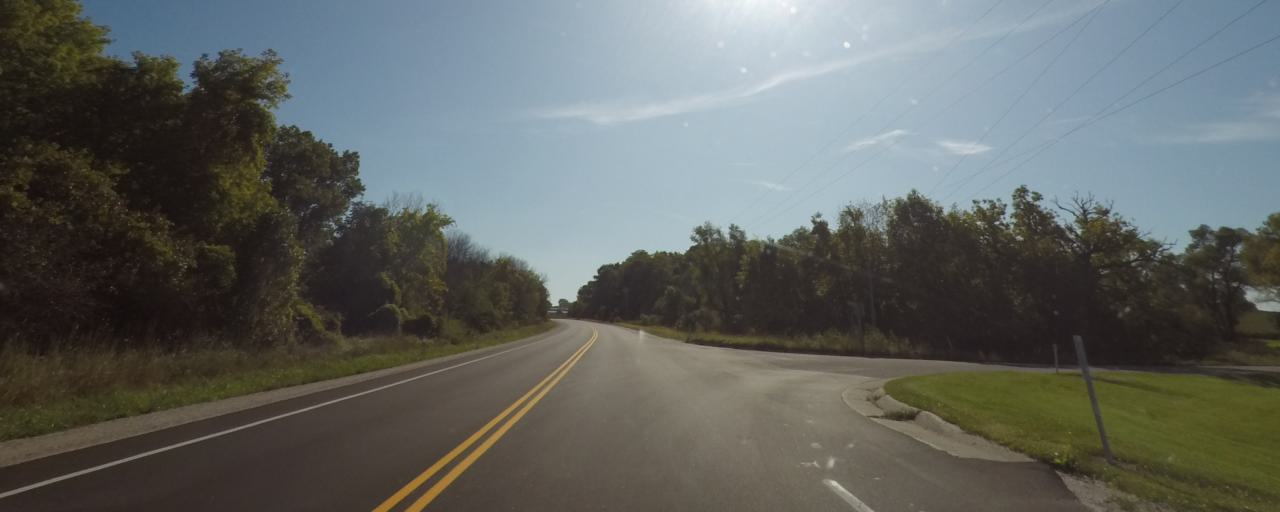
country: US
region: Wisconsin
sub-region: Jefferson County
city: Johnson Creek
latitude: 43.0112
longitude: -88.6625
